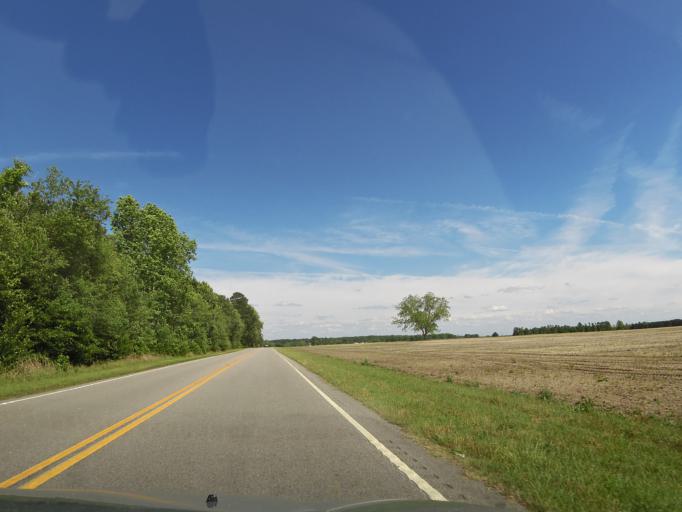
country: US
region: South Carolina
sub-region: Barnwell County
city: Blackville
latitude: 33.3714
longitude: -81.3436
